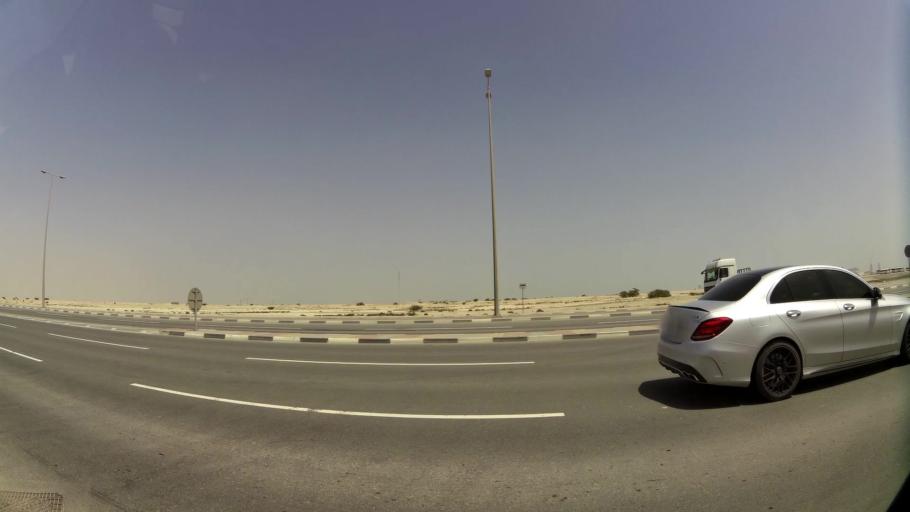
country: QA
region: Baladiyat Umm Salal
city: Umm Salal Muhammad
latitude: 25.3918
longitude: 51.4639
